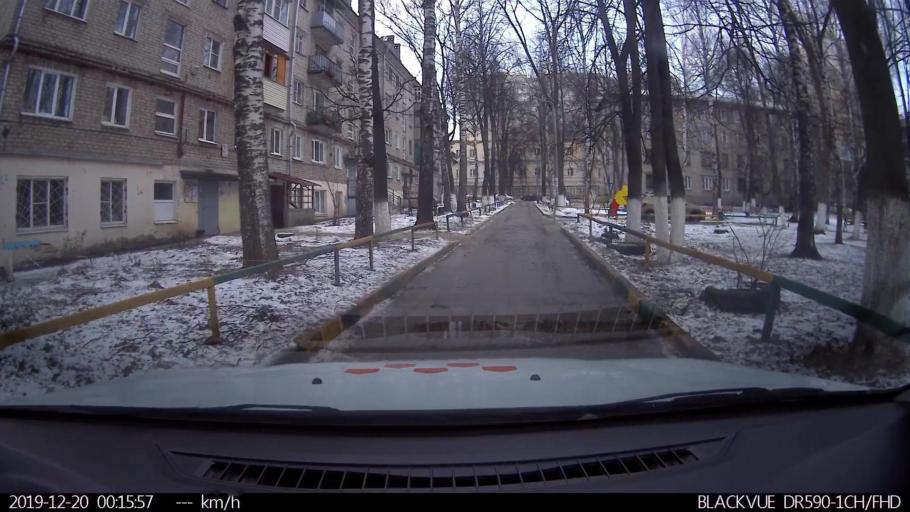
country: RU
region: Jaroslavl
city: Porech'ye-Rybnoye
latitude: 56.9712
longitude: 39.3962
